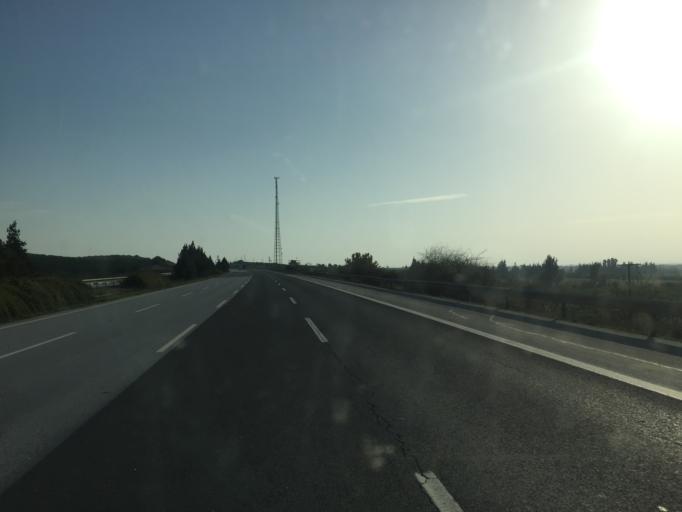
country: TR
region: Mersin
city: Yenice
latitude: 37.0226
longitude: 35.0807
